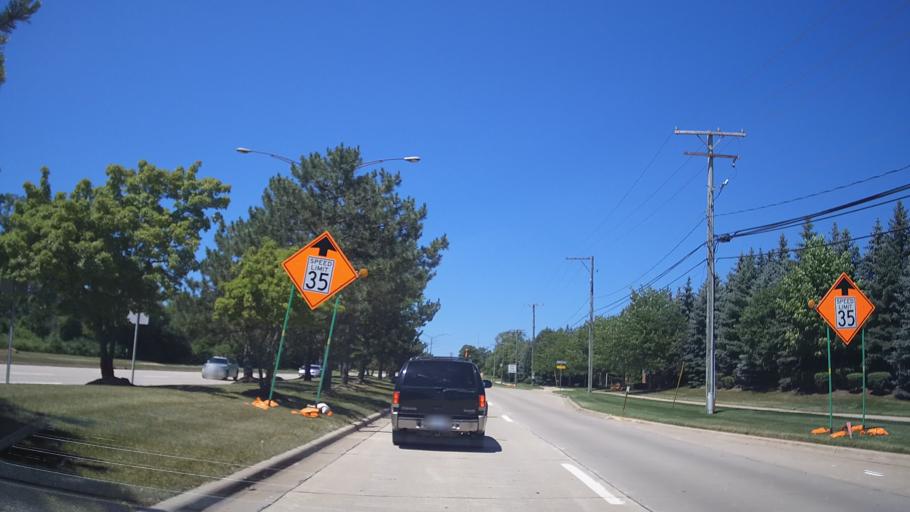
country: US
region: Michigan
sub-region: Oakland County
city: Troy
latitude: 42.5916
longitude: -83.1520
